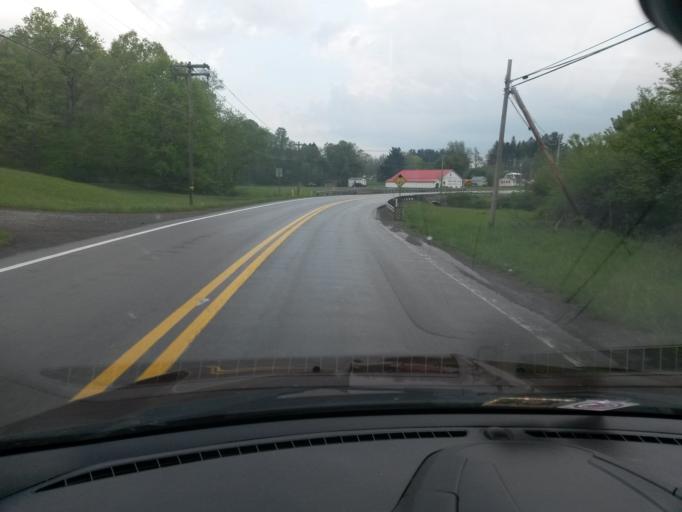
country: US
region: West Virginia
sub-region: Randolph County
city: Elkins
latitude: 38.7939
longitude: -79.9030
